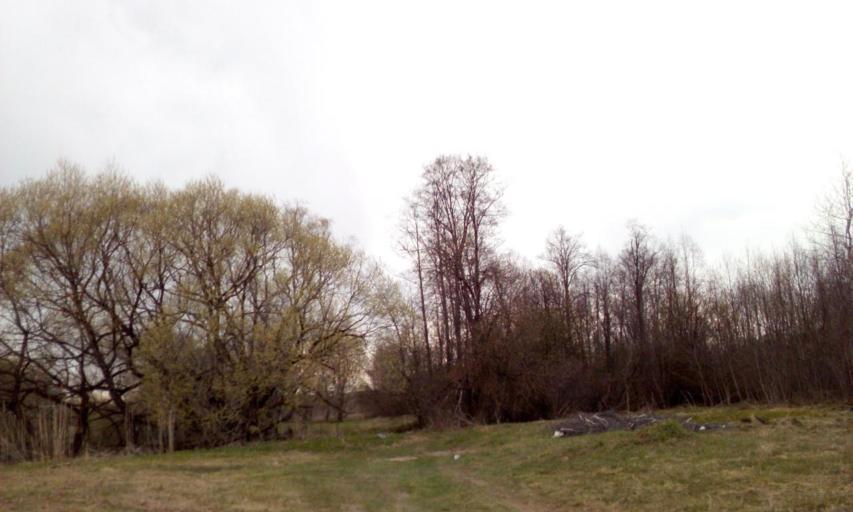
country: RU
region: Moskovskaya
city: Troitsk
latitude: 55.5140
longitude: 37.2706
